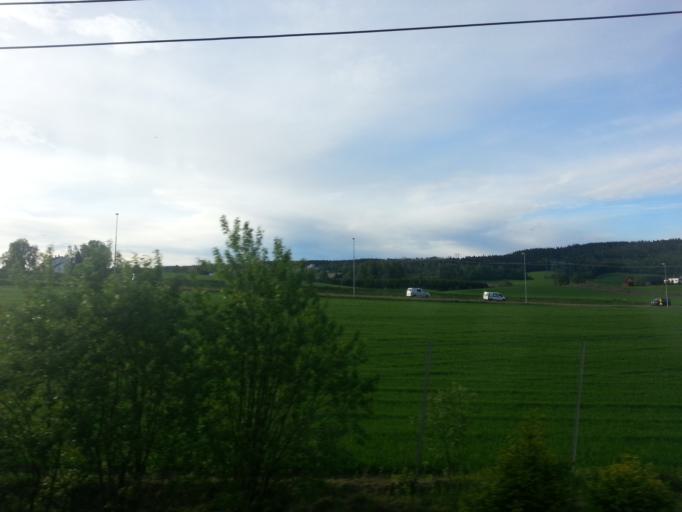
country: NO
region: Akershus
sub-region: Sorum
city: Frogner
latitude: 60.0142
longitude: 11.1107
